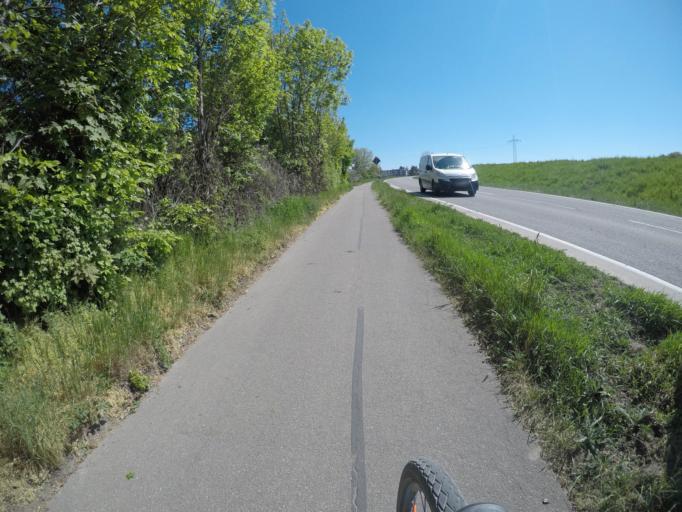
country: DE
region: Baden-Wuerttemberg
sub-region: Regierungsbezirk Stuttgart
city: Waiblingen
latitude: 48.8612
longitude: 9.2903
